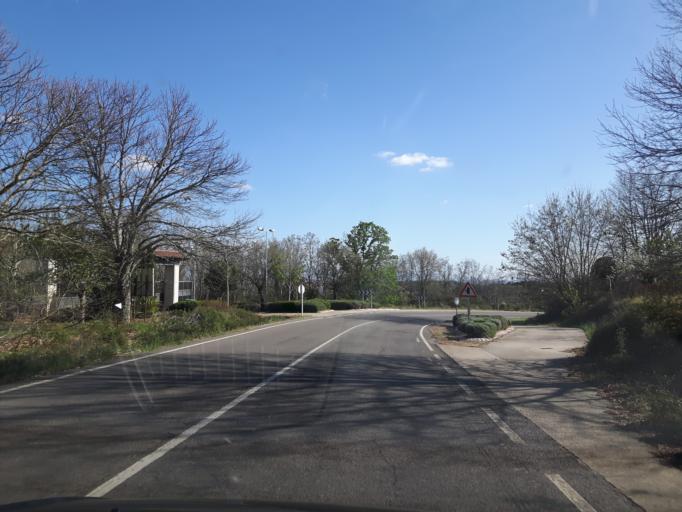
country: ES
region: Castille and Leon
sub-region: Provincia de Salamanca
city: San Miguel de Valero
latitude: 40.5503
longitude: -5.9159
